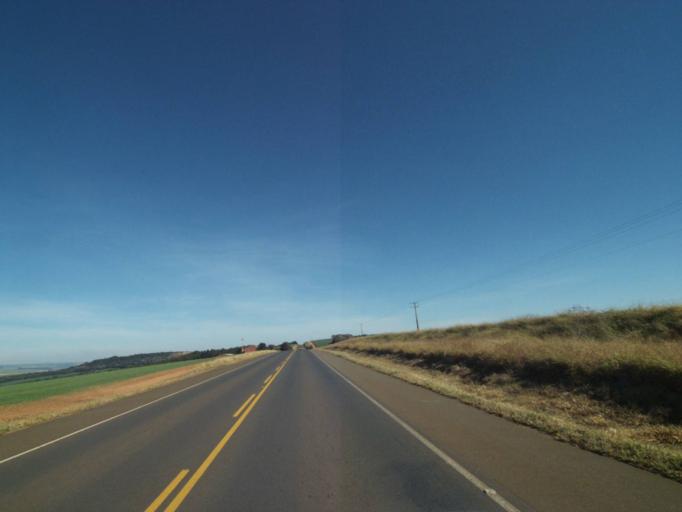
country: BR
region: Parana
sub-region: Tibagi
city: Tibagi
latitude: -24.3551
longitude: -50.3165
